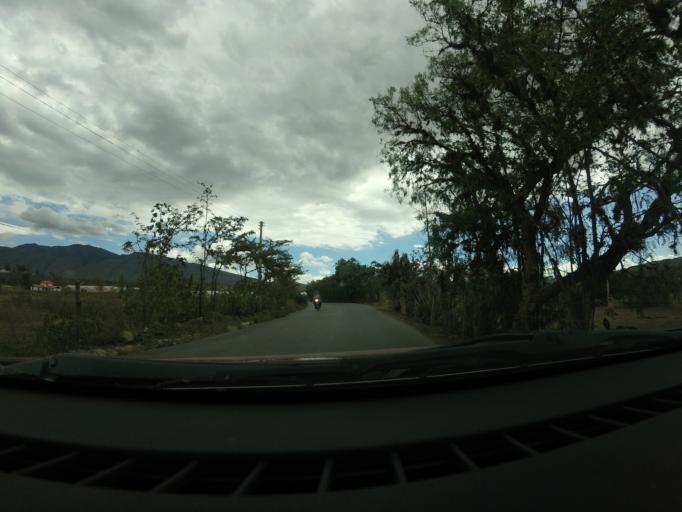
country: CO
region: Boyaca
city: Villa de Leiva
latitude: 5.6385
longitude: -73.5620
